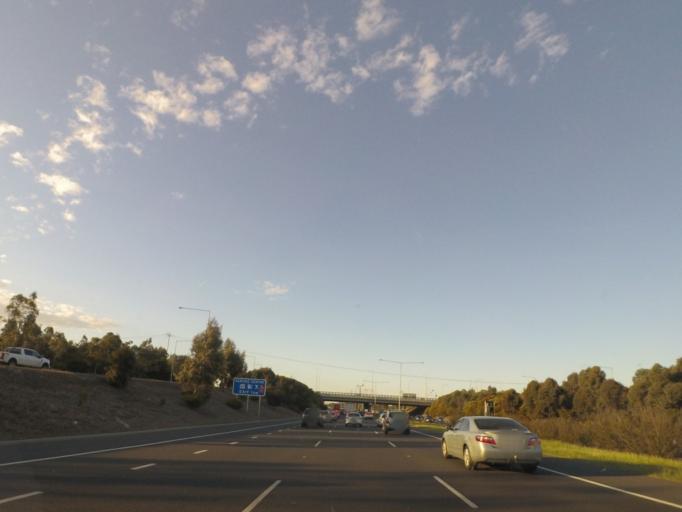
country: AU
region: Victoria
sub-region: Monash
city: Mulgrave
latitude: -37.9272
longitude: 145.2121
